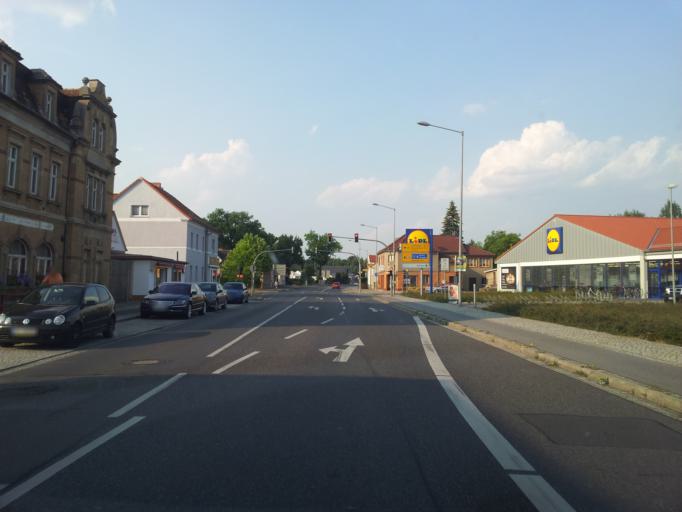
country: DE
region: Saxony
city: Bernsdorf
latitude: 51.3754
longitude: 14.0698
